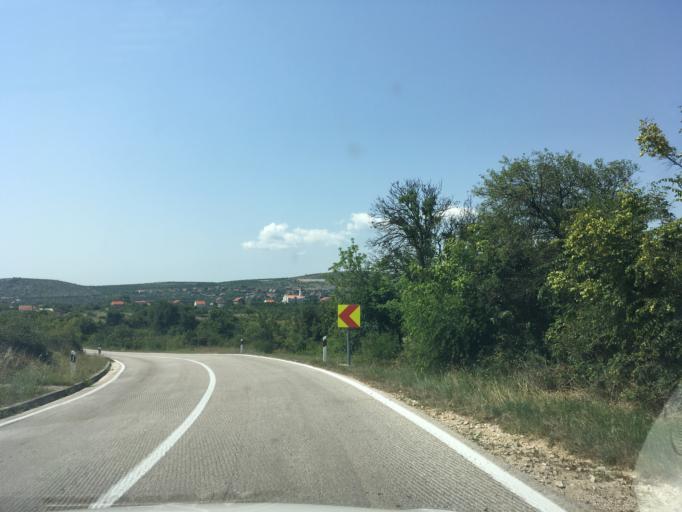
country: HR
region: Sibensko-Kniniska
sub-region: Grad Sibenik
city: Pirovac
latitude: 43.9590
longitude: 15.7725
